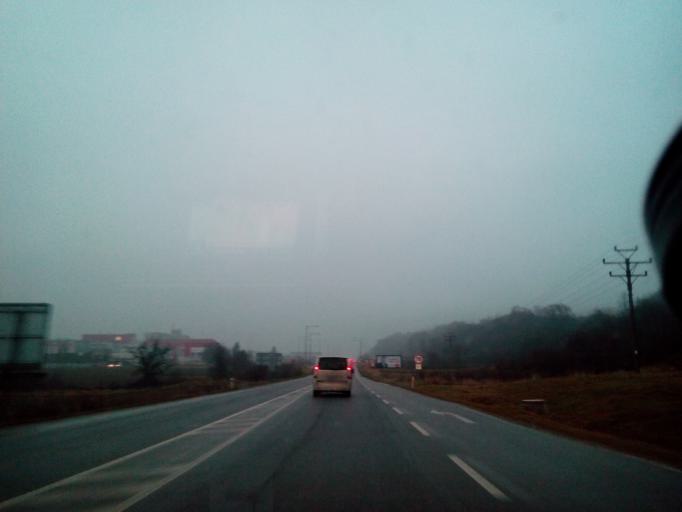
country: SK
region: Presovsky
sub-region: Okres Presov
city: Presov
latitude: 49.0415
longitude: 21.2124
